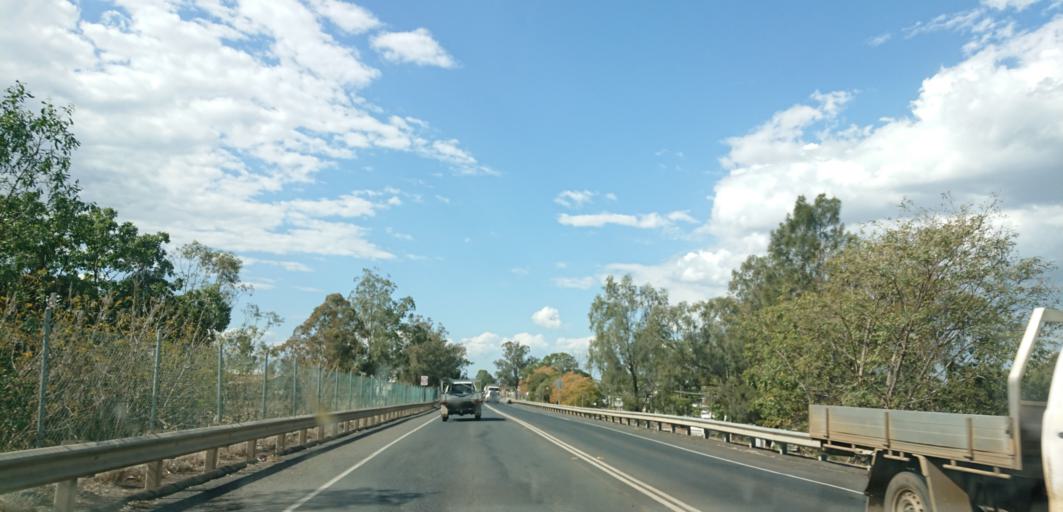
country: AU
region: Queensland
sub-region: Lockyer Valley
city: Gatton
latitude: -27.5564
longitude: 152.2861
